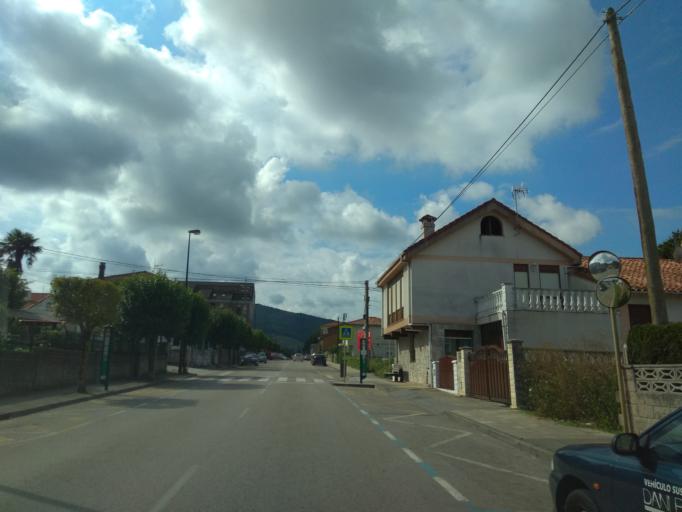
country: ES
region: Cantabria
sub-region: Provincia de Cantabria
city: Torrelavega
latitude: 43.3370
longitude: -4.0451
